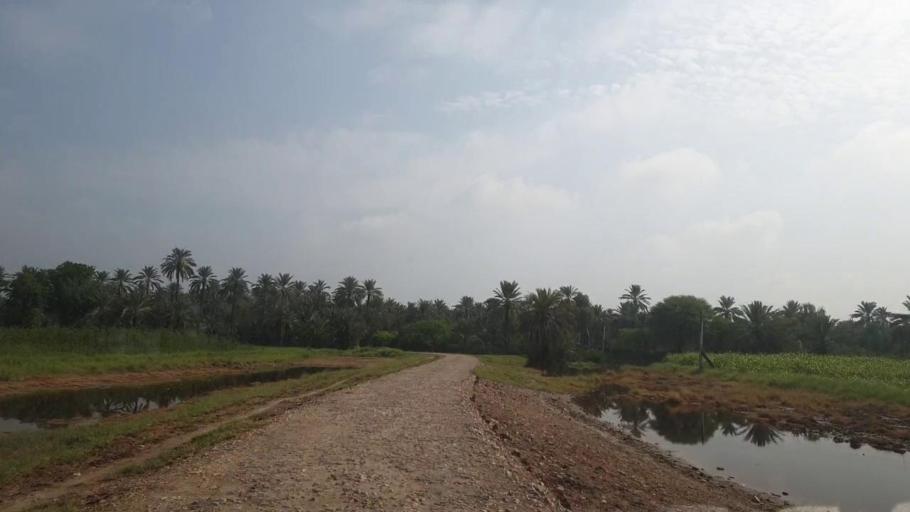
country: PK
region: Sindh
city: Khairpur
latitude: 27.5810
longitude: 68.7688
